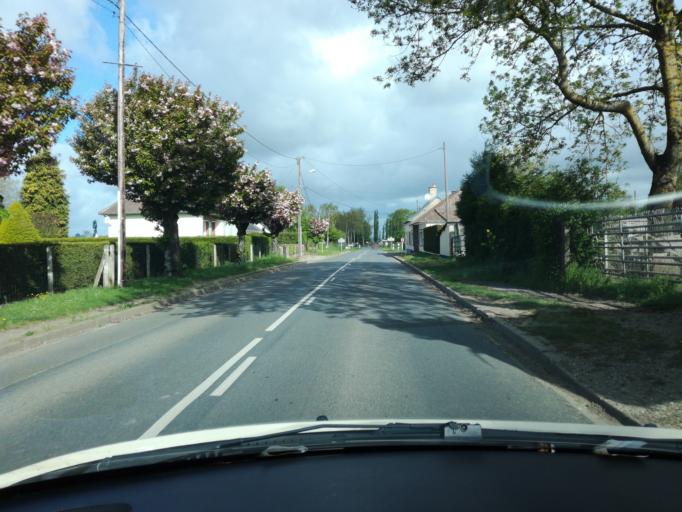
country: FR
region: Picardie
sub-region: Departement de la Somme
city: Hornoy-le-Bourg
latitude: 49.8477
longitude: 1.8974
